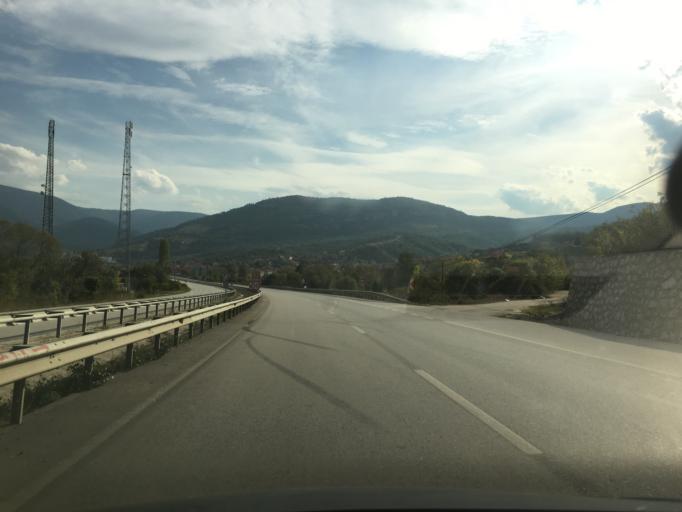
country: TR
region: Karabuk
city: Karabuk
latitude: 41.1107
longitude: 32.6691
